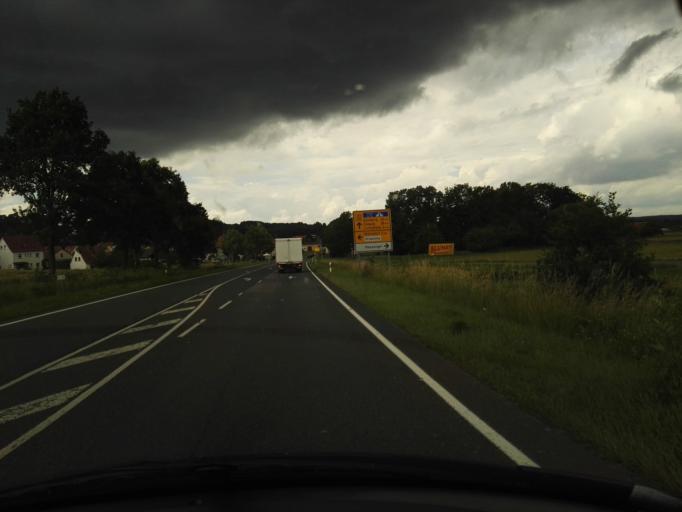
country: DE
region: Bavaria
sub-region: Upper Franconia
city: Hochstadt am Main
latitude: 50.1456
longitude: 11.1448
